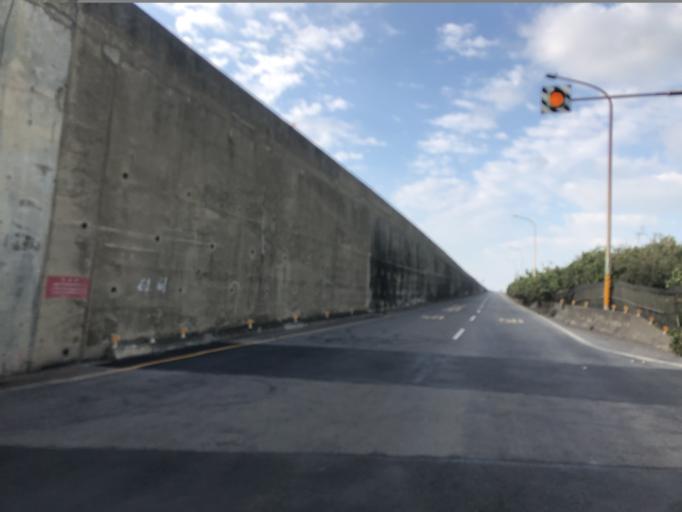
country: TW
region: Taiwan
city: Taoyuan City
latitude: 25.0695
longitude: 121.1212
